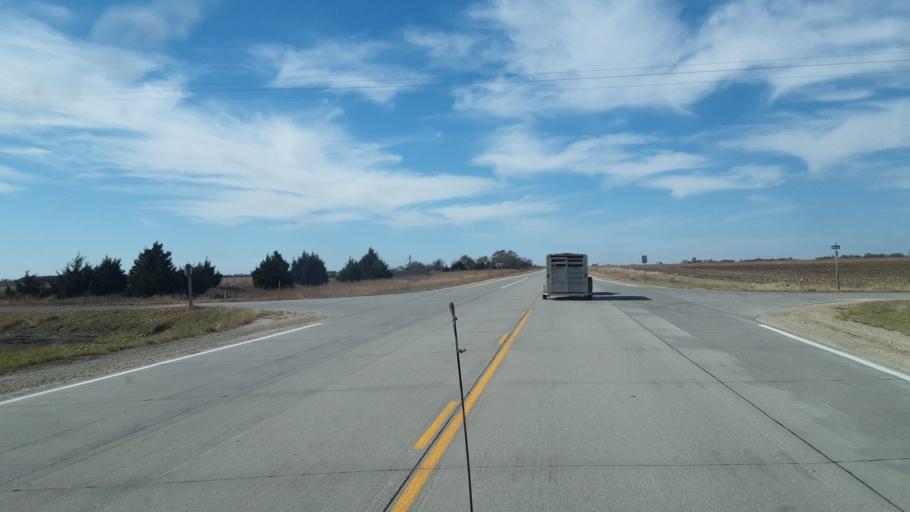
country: US
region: Kansas
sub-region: Marion County
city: Marion
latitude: 38.3550
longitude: -97.0957
